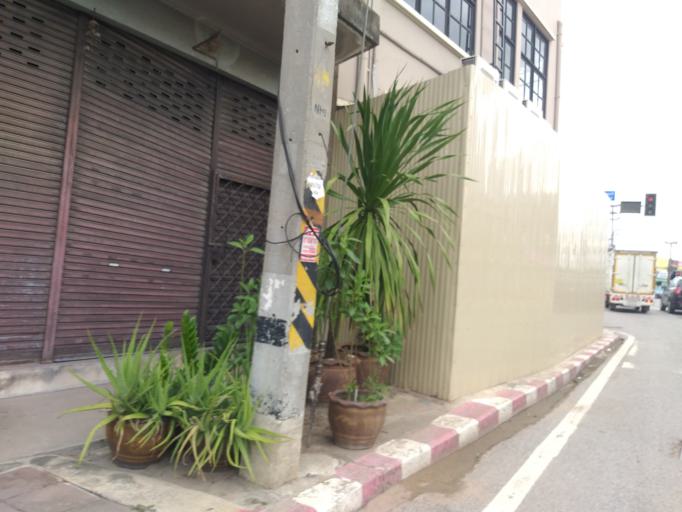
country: TH
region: Nakhon Ratchasima
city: Nakhon Ratchasima
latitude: 14.9742
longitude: 102.0842
